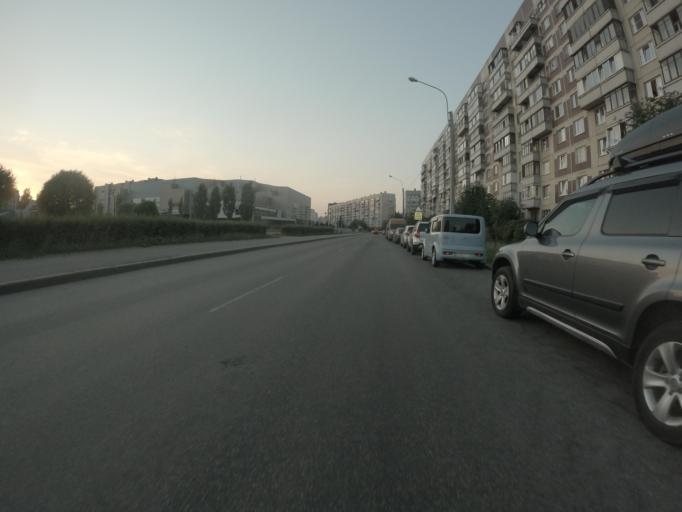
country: RU
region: St.-Petersburg
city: Krasnogvargeisky
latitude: 59.9185
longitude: 30.4528
